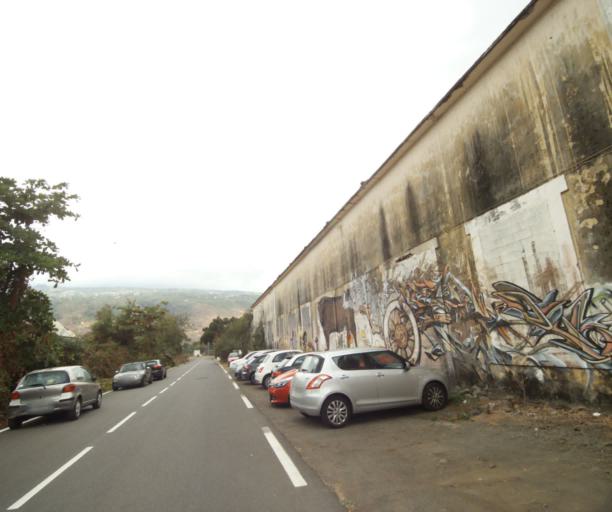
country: RE
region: Reunion
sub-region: Reunion
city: Saint-Paul
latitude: -20.9883
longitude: 55.2985
